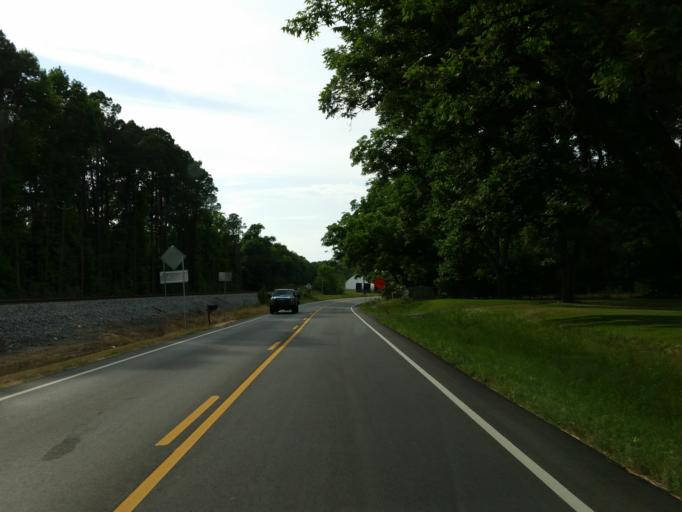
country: US
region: Georgia
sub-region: Turner County
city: Ashburn
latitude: 31.7197
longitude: -83.6623
